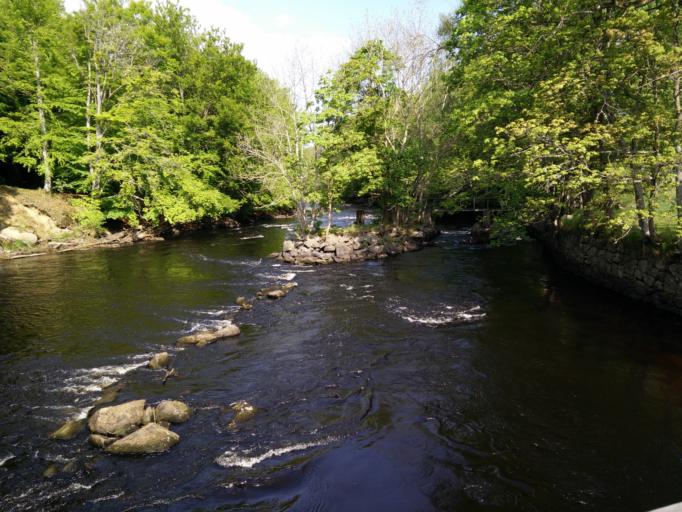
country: SE
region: Blekinge
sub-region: Karlshamns Kommun
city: Morrum
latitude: 56.2017
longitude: 14.7516
